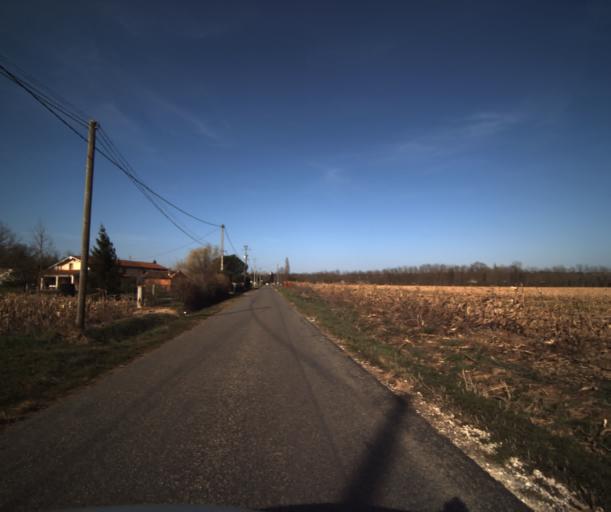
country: FR
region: Midi-Pyrenees
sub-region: Departement du Tarn-et-Garonne
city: Labastide-Saint-Pierre
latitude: 43.9250
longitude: 1.3534
